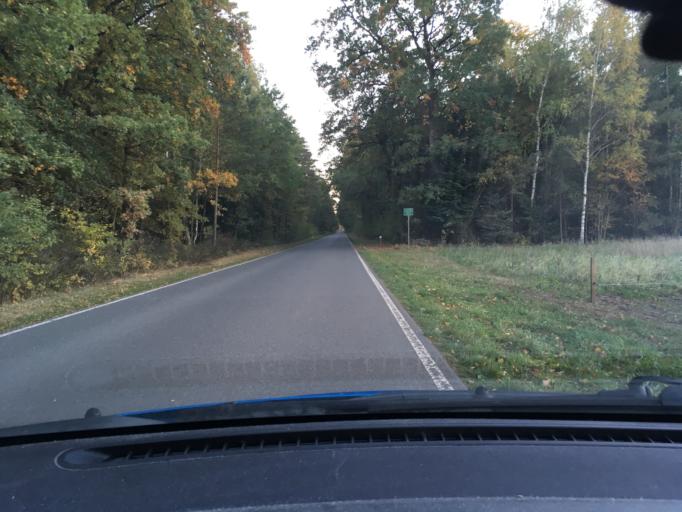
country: DE
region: Lower Saxony
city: Neetze
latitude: 53.2938
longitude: 10.6164
